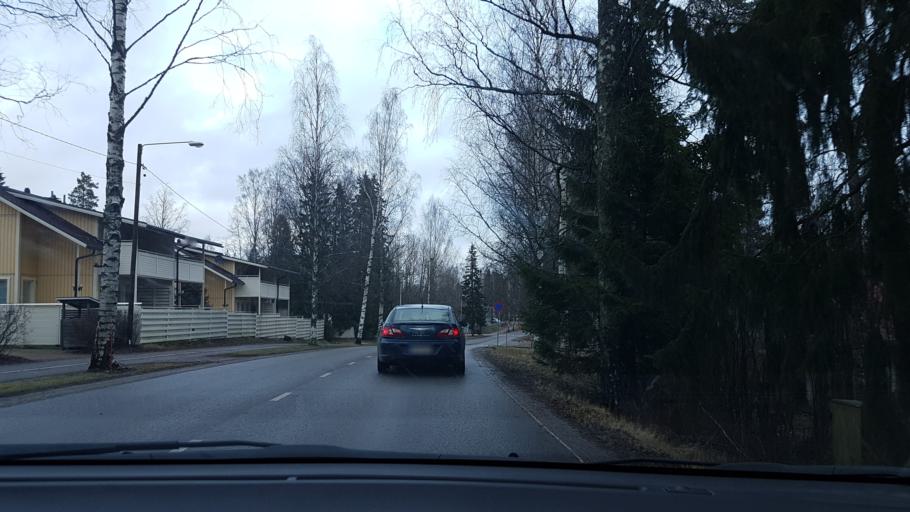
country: FI
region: Uusimaa
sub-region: Helsinki
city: Kerava
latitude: 60.3763
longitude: 25.0804
